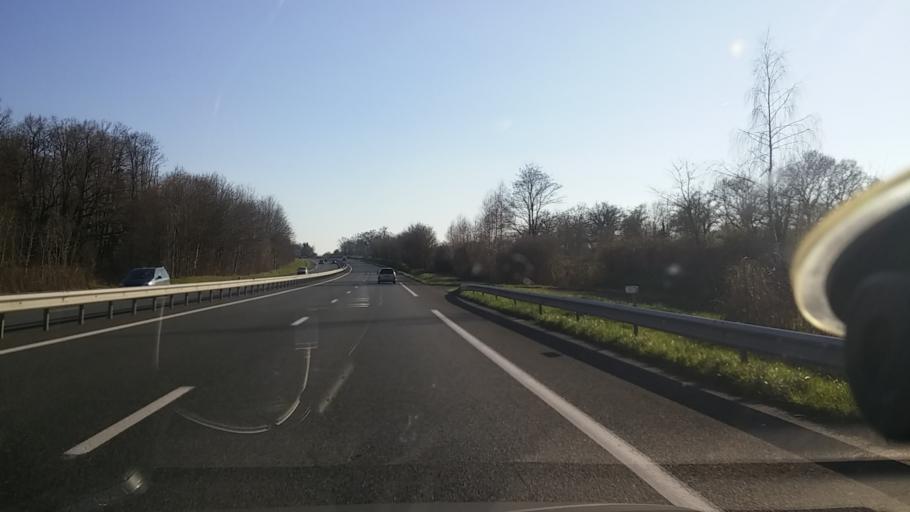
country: FR
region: Centre
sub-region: Departement de l'Indre
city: Chantome
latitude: 46.4284
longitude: 1.4751
